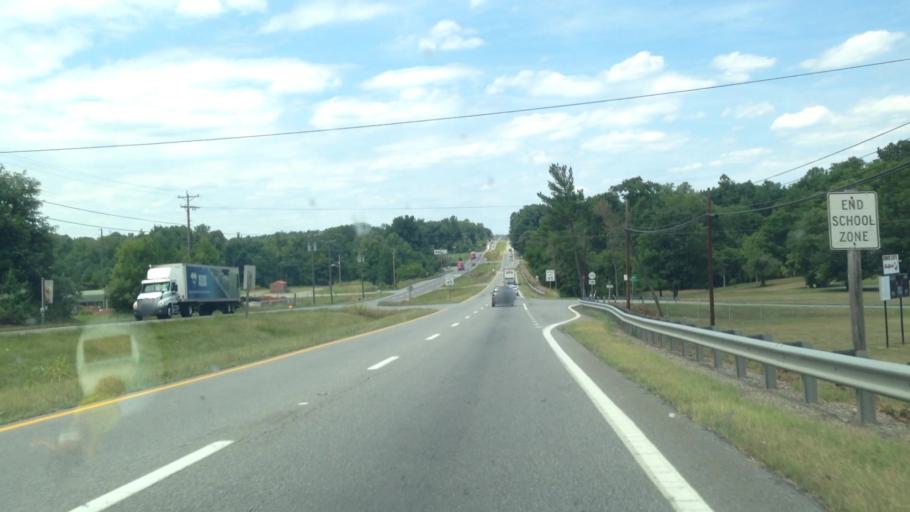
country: US
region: Virginia
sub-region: Henry County
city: Chatmoss
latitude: 36.6095
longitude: -79.8611
